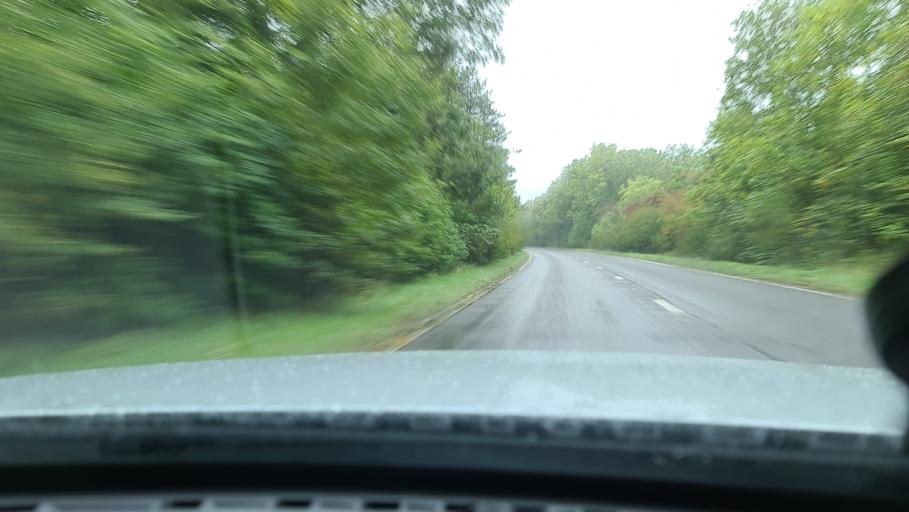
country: GB
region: England
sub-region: Oxfordshire
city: Deddington
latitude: 51.9436
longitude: -1.3240
